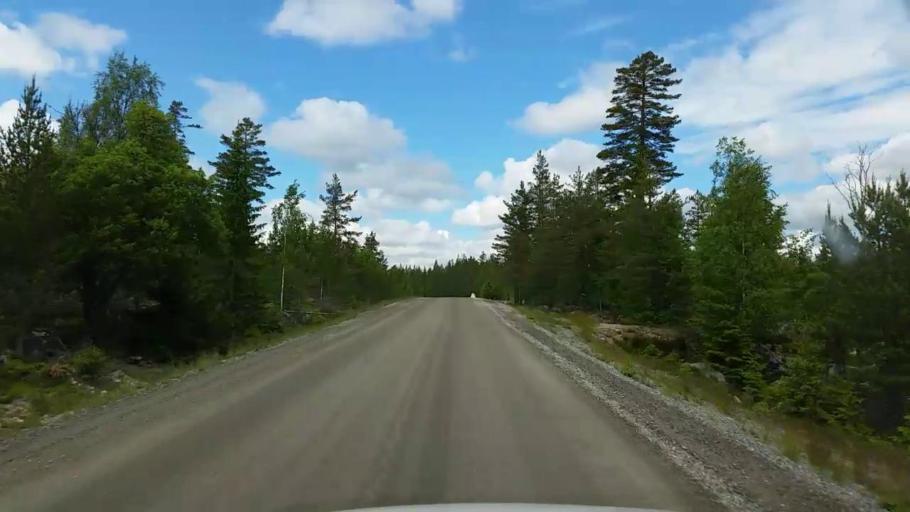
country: SE
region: Gaevleborg
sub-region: Bollnas Kommun
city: Kilafors
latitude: 61.0158
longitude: 16.3837
